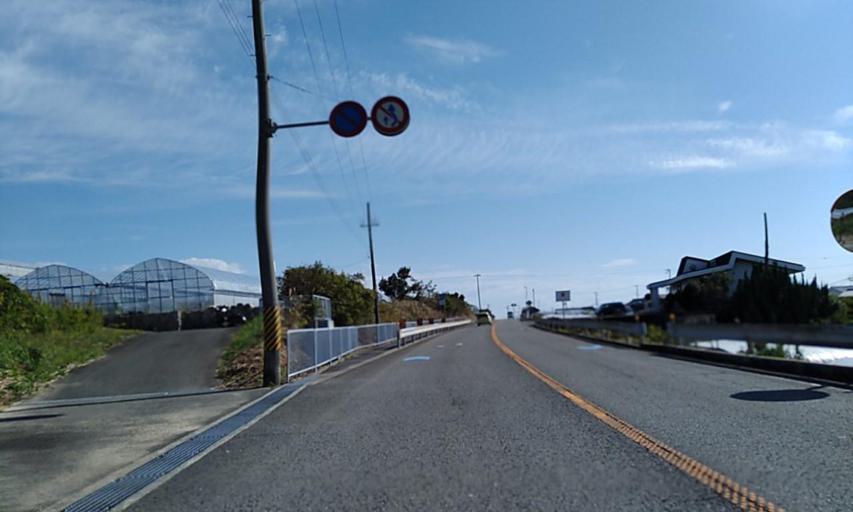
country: JP
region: Wakayama
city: Gobo
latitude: 33.8246
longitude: 135.1900
